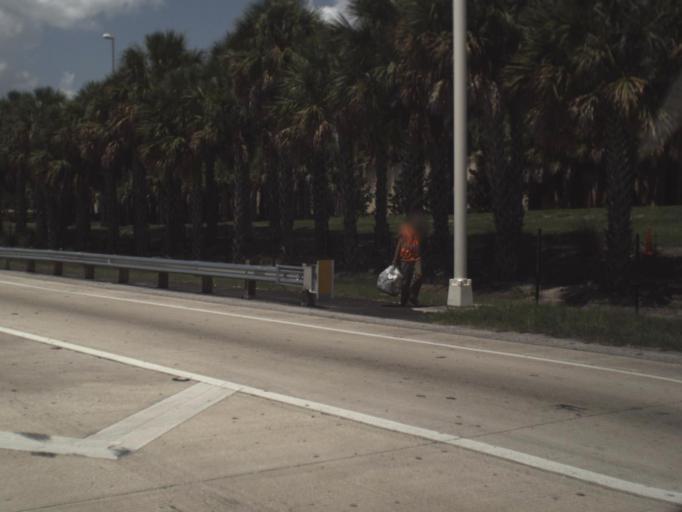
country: US
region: Florida
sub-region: Hillsborough County
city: Tampa
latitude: 27.9653
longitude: -82.4407
